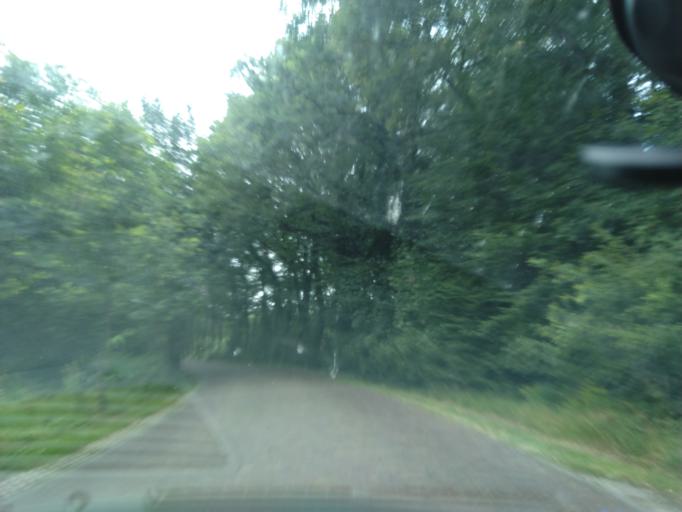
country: NL
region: Groningen
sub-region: Gemeente Vlagtwedde
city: Vlagtwedde
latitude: 53.0942
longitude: 7.1433
